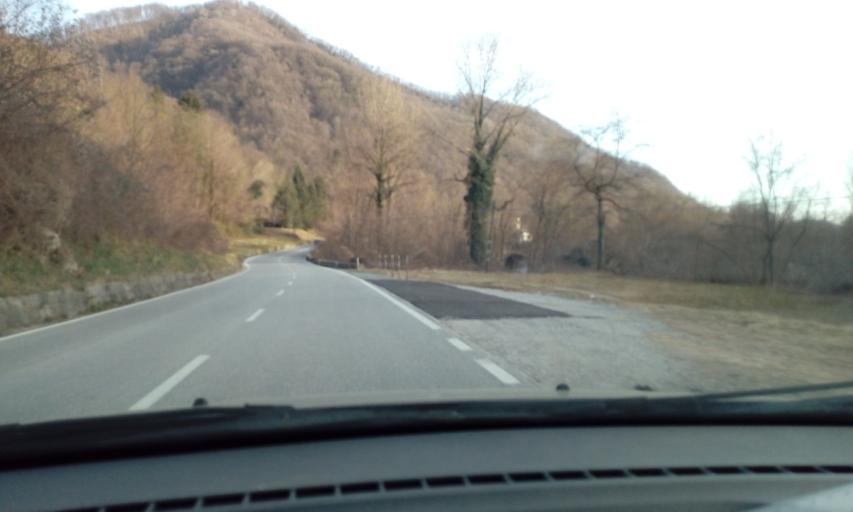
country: IT
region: Friuli Venezia Giulia
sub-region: Provincia di Udine
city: Pulfero
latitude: 46.1717
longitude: 13.4875
